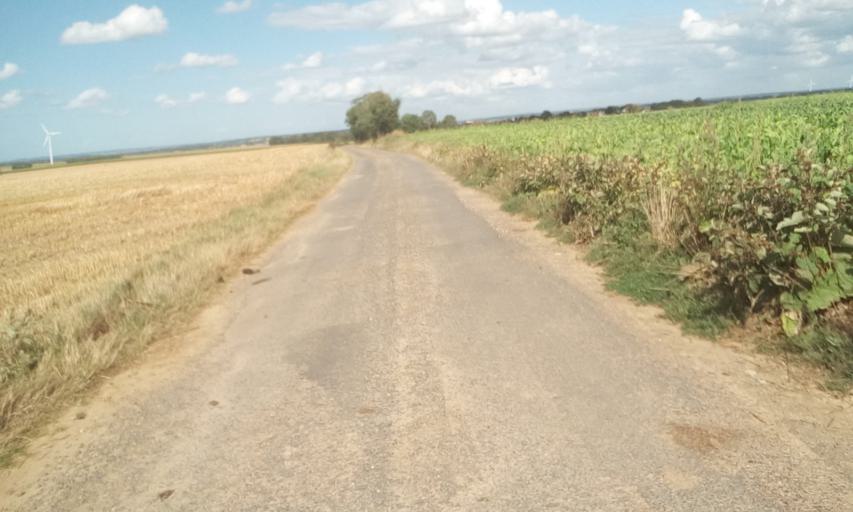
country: FR
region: Lower Normandy
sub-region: Departement du Calvados
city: Saint-Sylvain
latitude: 49.0759
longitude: -0.2389
